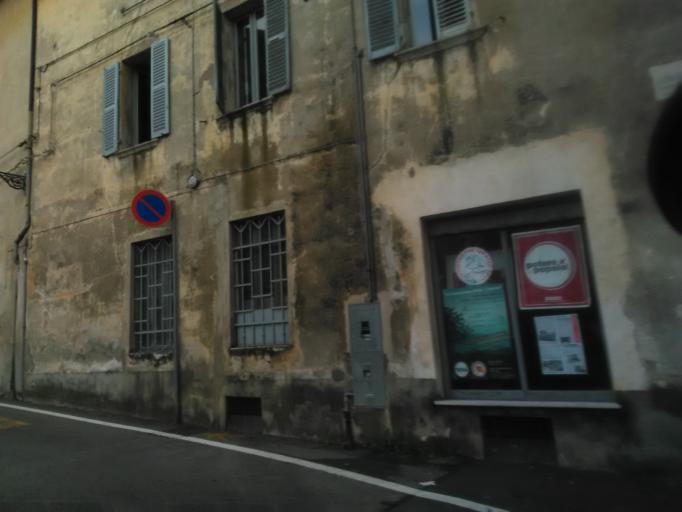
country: IT
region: Piedmont
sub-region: Provincia di Vercelli
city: Varallo
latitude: 45.8167
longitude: 8.2535
